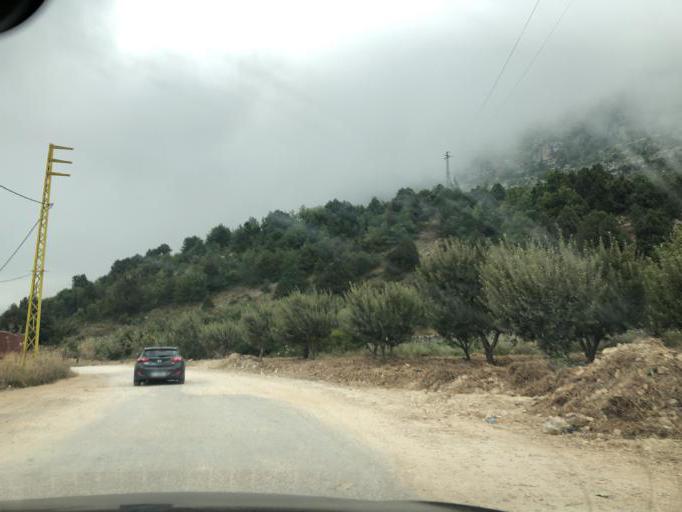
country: LB
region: Liban-Nord
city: Bcharre
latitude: 34.0845
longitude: 35.8881
